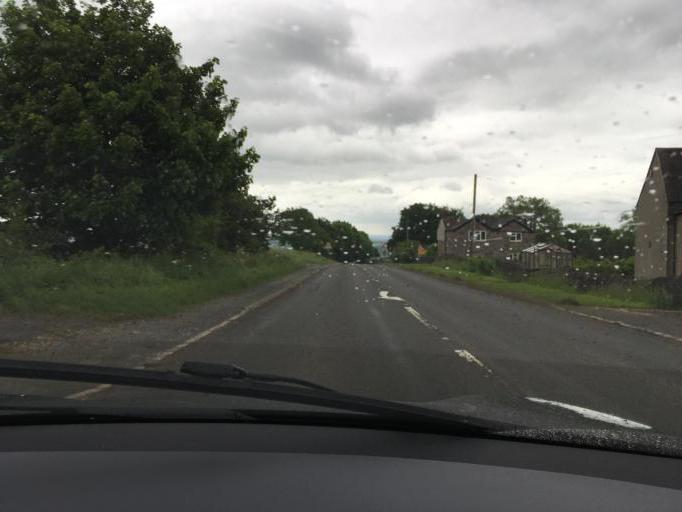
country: GB
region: England
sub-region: Staffordshire
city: Mayfield
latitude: 53.0279
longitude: -1.7965
